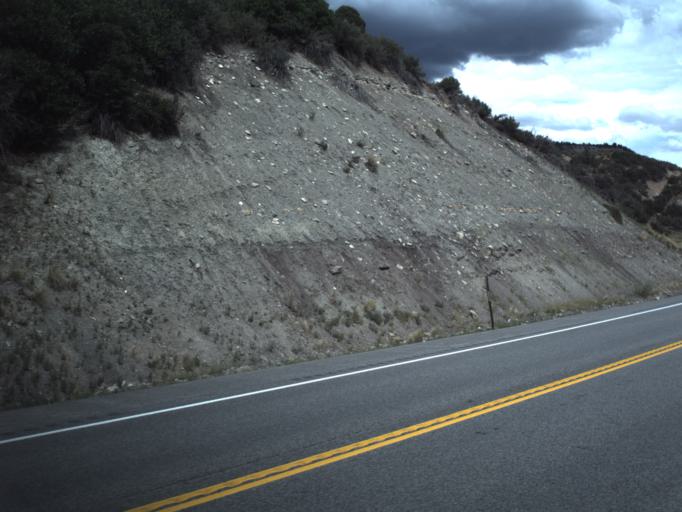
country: US
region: Utah
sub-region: Carbon County
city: Helper
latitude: 39.9339
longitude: -111.1270
